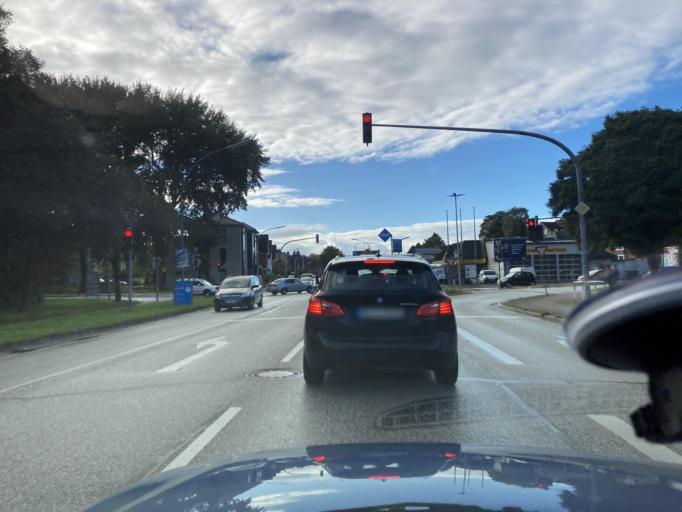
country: DE
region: Schleswig-Holstein
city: Rendsburg
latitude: 54.3078
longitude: 9.6500
